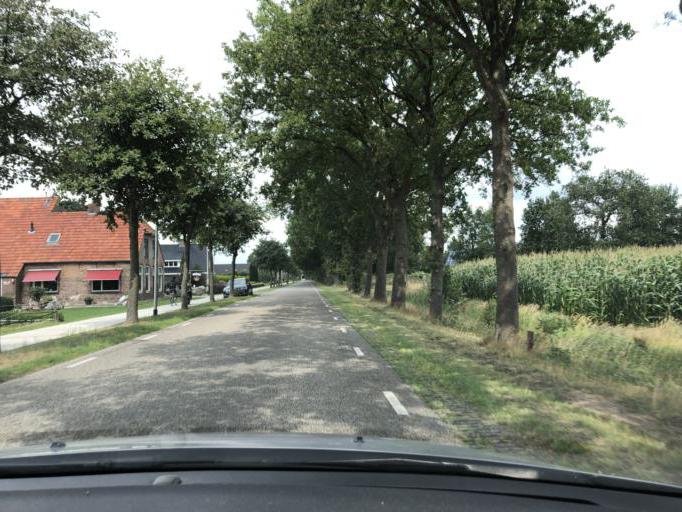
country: NL
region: Drenthe
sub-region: Gemeente Hoogeveen
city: Hoogeveen
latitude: 52.6791
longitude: 6.4859
